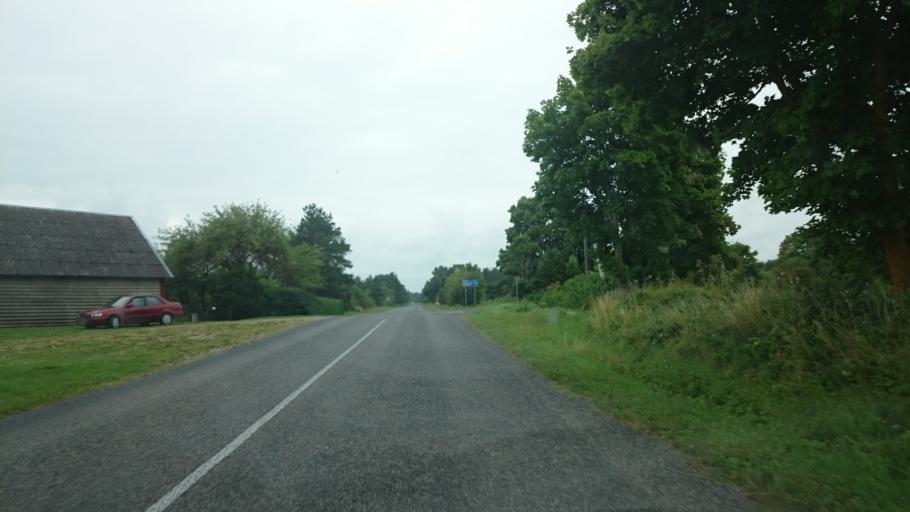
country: EE
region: Saare
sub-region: Orissaare vald
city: Orissaare
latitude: 58.5817
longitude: 23.0271
